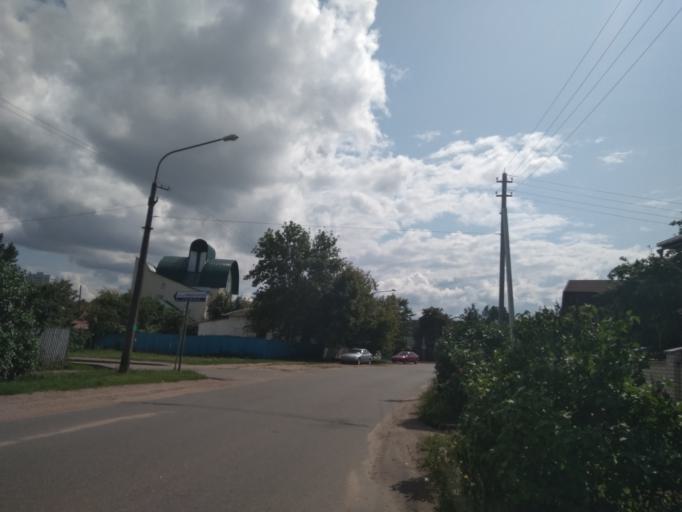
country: BY
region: Minsk
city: Minsk
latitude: 53.9355
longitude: 27.5551
